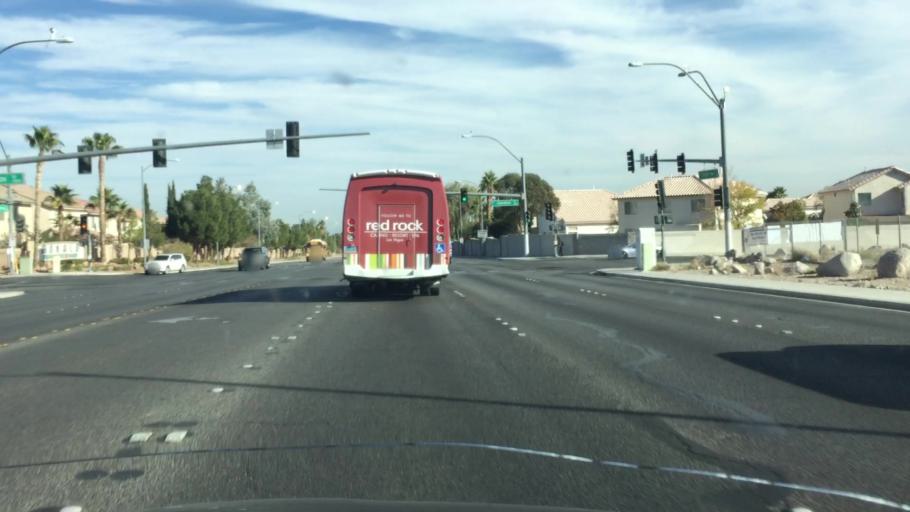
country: US
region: Nevada
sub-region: Clark County
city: Spring Valley
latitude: 36.1293
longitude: -115.2705
